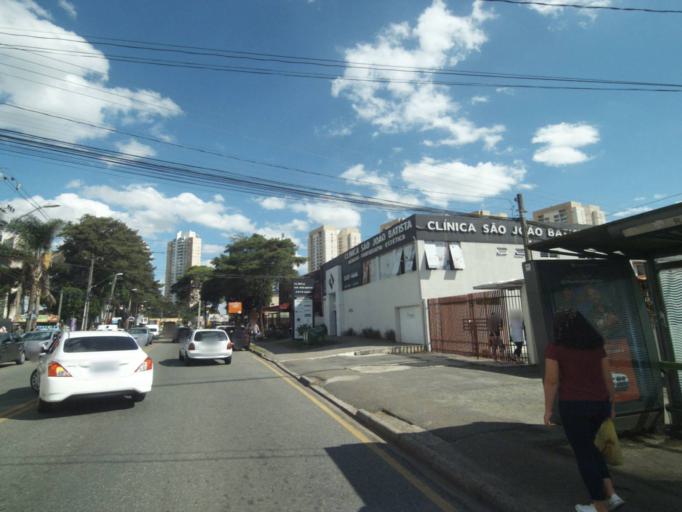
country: BR
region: Parana
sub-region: Curitiba
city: Curitiba
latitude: -25.4383
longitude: -49.3475
